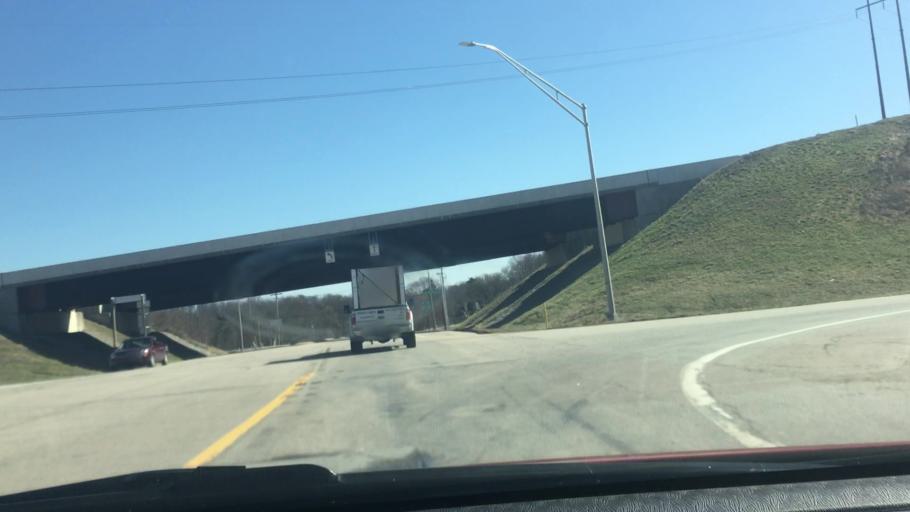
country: US
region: Pennsylvania
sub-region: Washington County
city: Baidland
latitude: 40.1972
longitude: -79.9885
